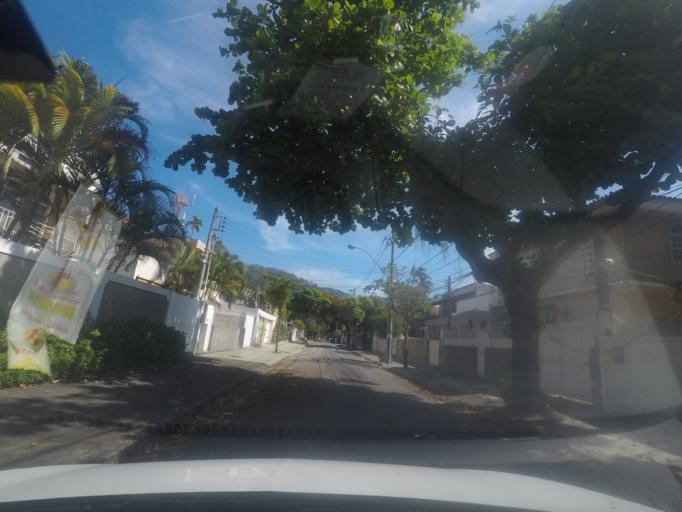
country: BR
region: Rio de Janeiro
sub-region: Niteroi
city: Niteroi
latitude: -22.9152
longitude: -43.0928
